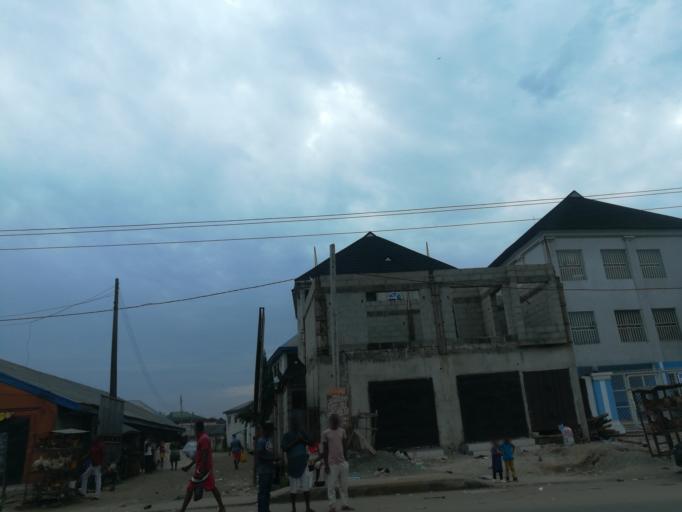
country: NG
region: Rivers
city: Port Harcourt
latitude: 4.8171
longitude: 6.9549
